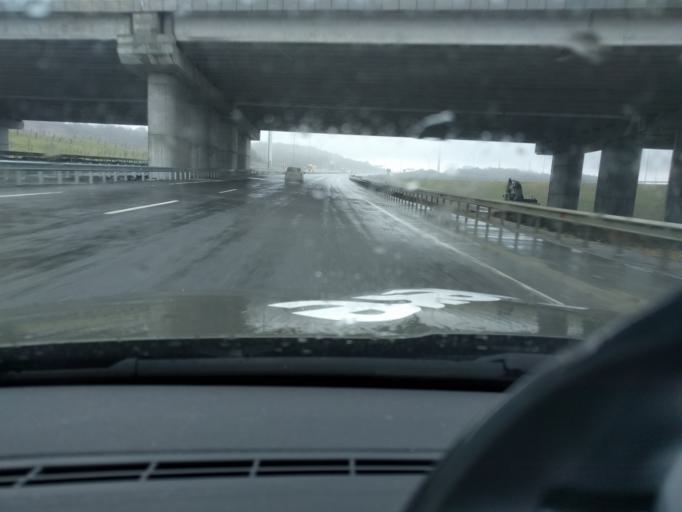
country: TR
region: Istanbul
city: Durusu
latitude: 41.2585
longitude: 28.6819
